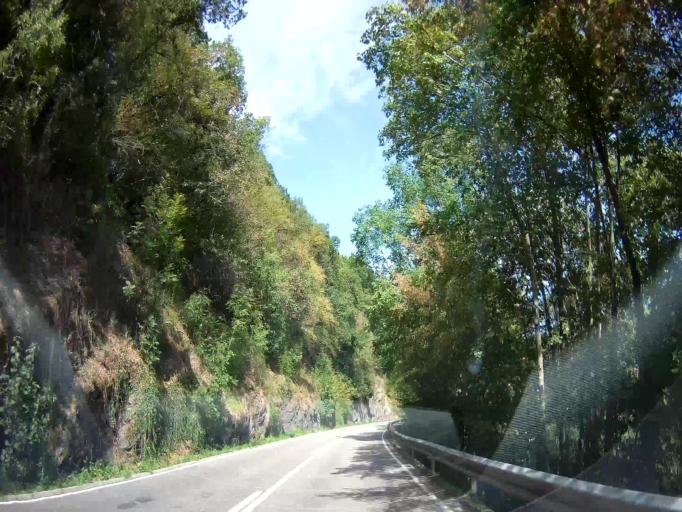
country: BE
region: Wallonia
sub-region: Province du Luxembourg
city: Rendeux
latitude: 50.2218
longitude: 5.5211
